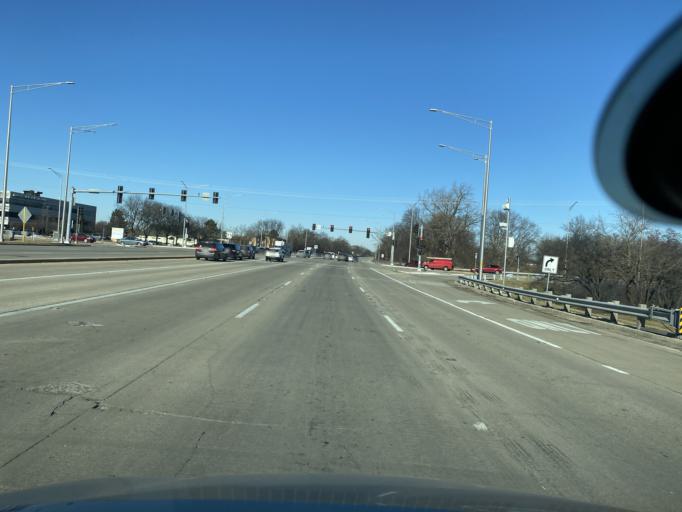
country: US
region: Illinois
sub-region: DuPage County
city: Willowbrook
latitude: 41.7734
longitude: -87.9463
